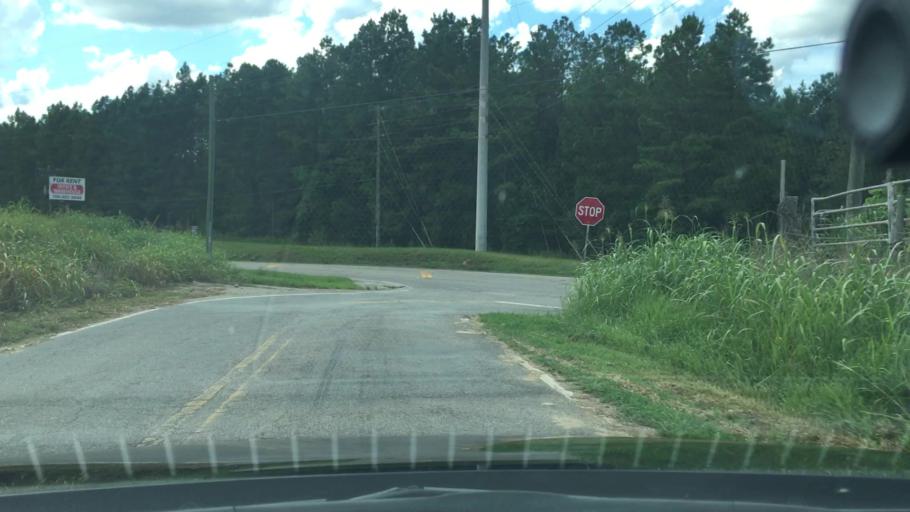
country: US
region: Georgia
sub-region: Putnam County
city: Jefferson
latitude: 33.3773
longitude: -83.3210
